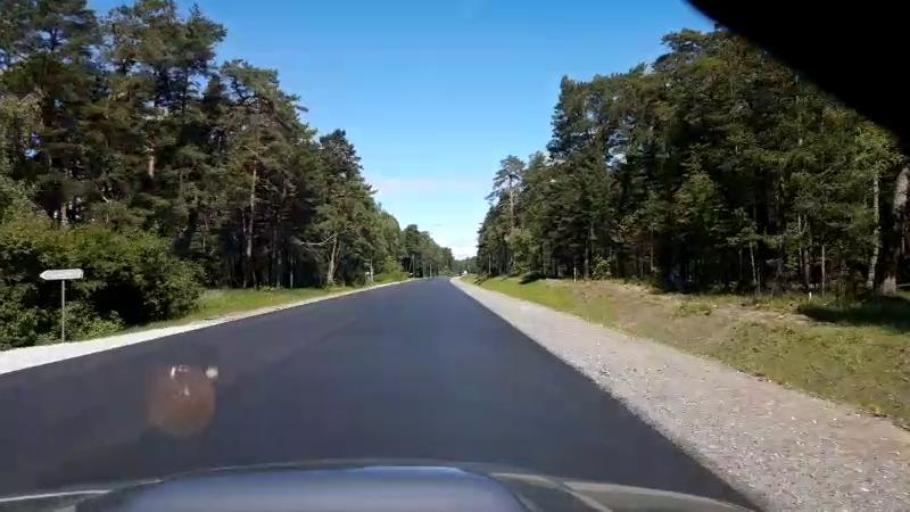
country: LV
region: Salacgrivas
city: Ainazi
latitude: 57.8145
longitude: 24.3473
